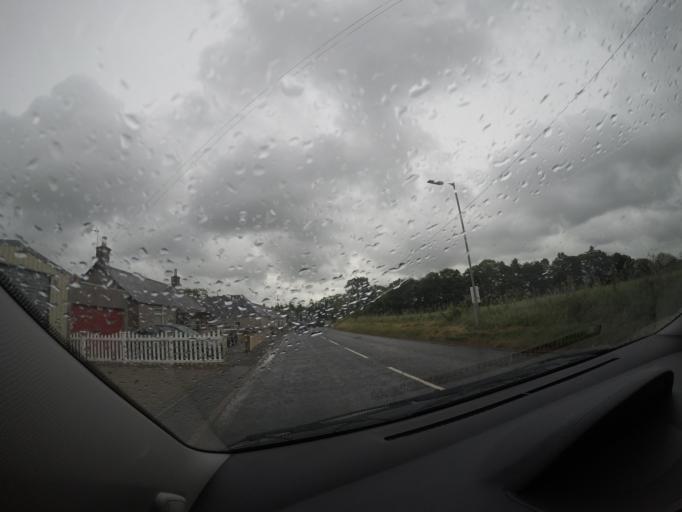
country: GB
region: Scotland
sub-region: Angus
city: Brechin
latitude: 56.7820
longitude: -2.6457
